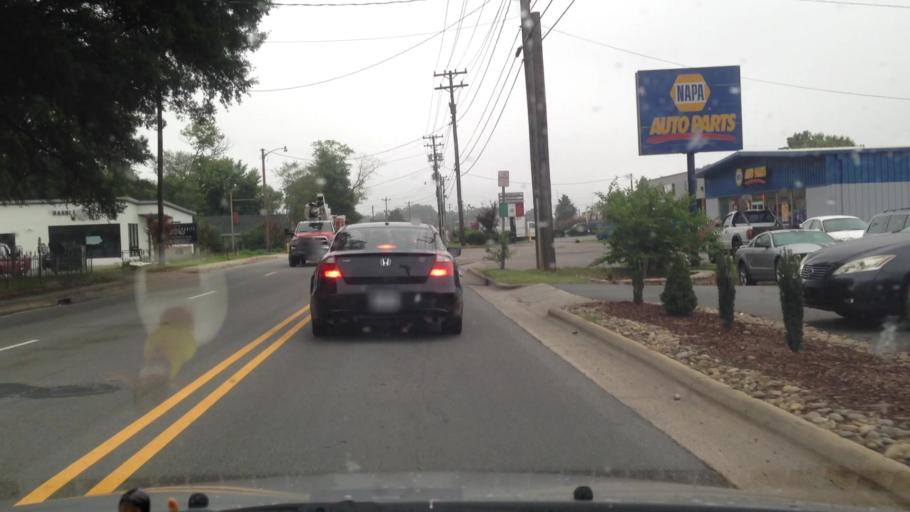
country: US
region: North Carolina
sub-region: Forsyth County
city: Kernersville
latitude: 36.1198
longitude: -80.0686
